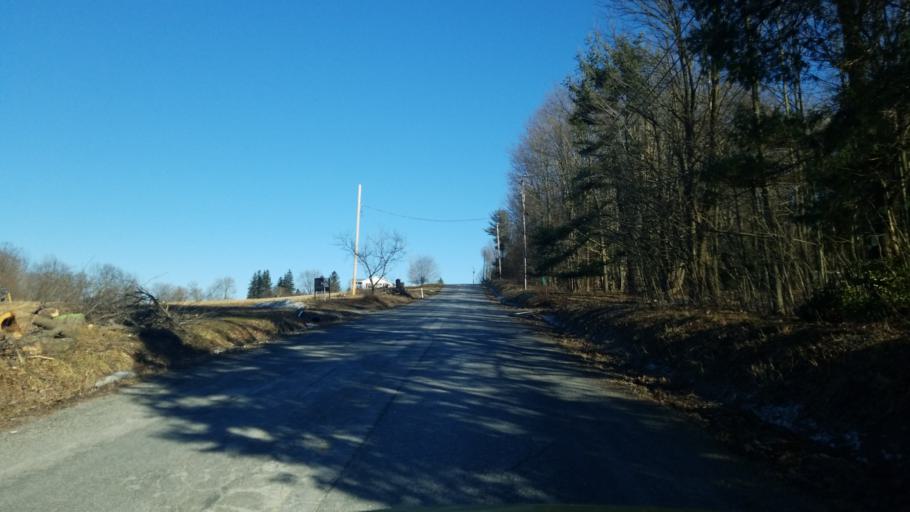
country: US
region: Pennsylvania
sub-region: Clearfield County
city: Sandy
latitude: 41.0535
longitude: -78.7286
